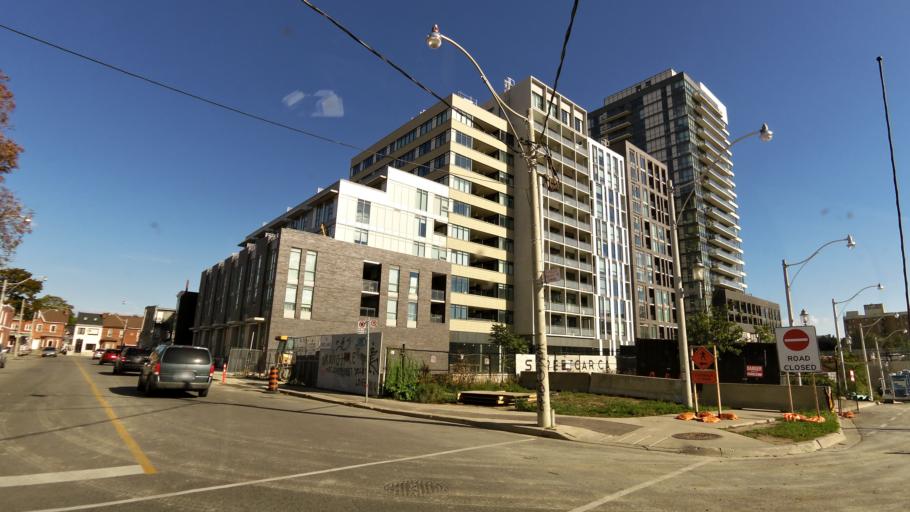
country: CA
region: Ontario
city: Toronto
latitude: 43.6438
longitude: -79.4292
